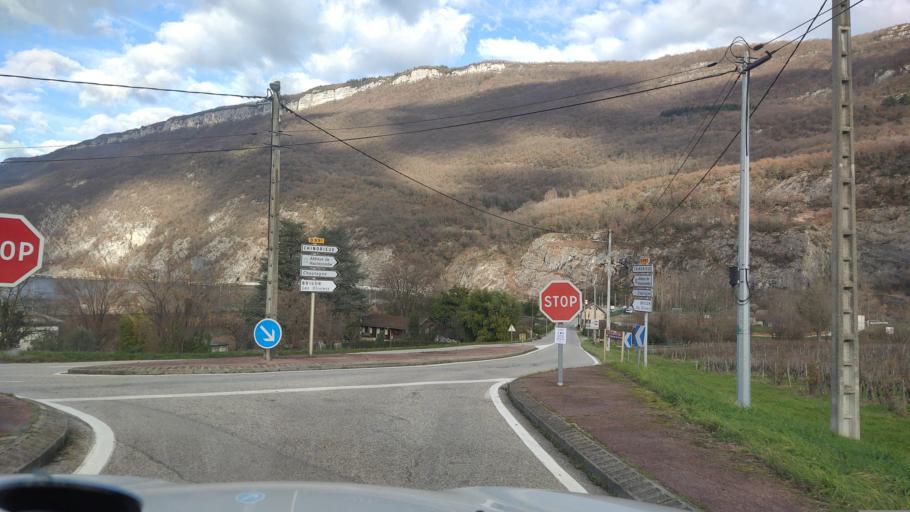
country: FR
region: Rhone-Alpes
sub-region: Departement de la Savoie
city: Brison-Saint-Innocent
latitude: 45.7326
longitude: 5.8894
